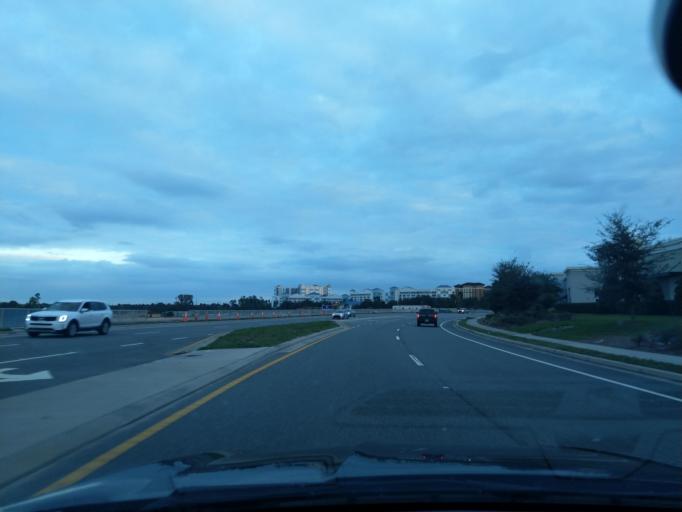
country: US
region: Florida
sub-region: Orange County
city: Williamsburg
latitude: 28.3943
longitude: -81.4842
